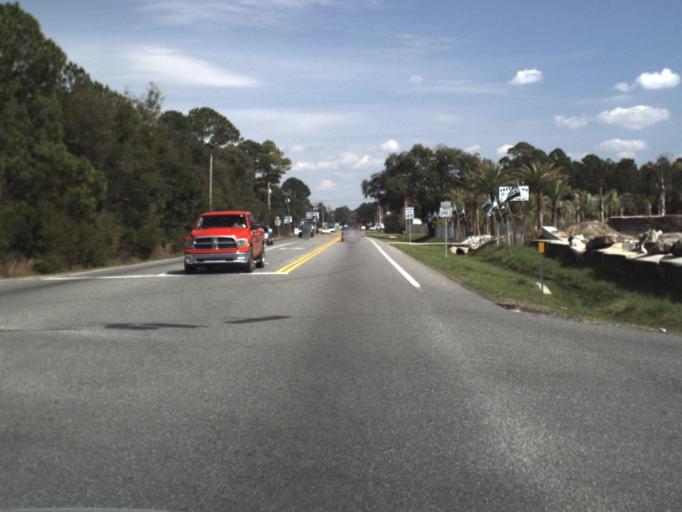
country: US
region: Florida
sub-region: Bay County
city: Pretty Bayou
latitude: 30.1945
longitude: -85.6918
